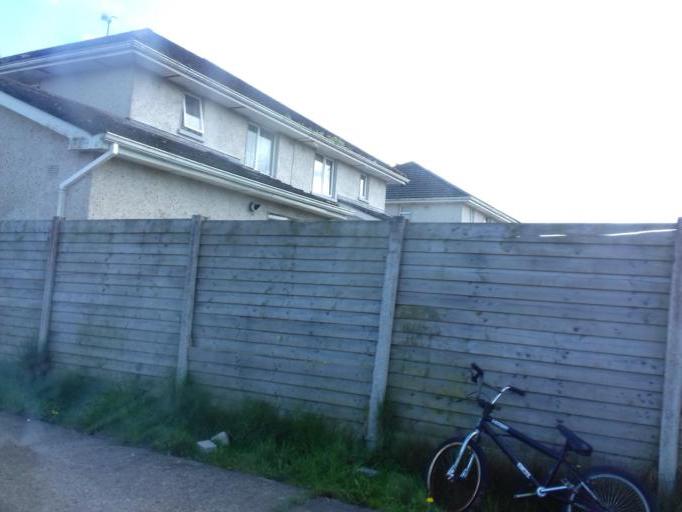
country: IE
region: Leinster
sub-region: Laois
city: Portlaoise
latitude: 53.0475
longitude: -7.2695
